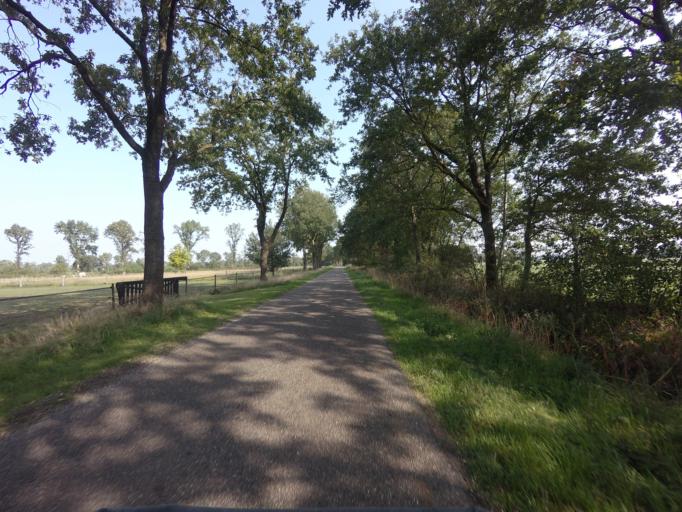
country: NL
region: Drenthe
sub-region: Gemeente Tynaarlo
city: Vries
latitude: 53.1308
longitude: 6.5272
